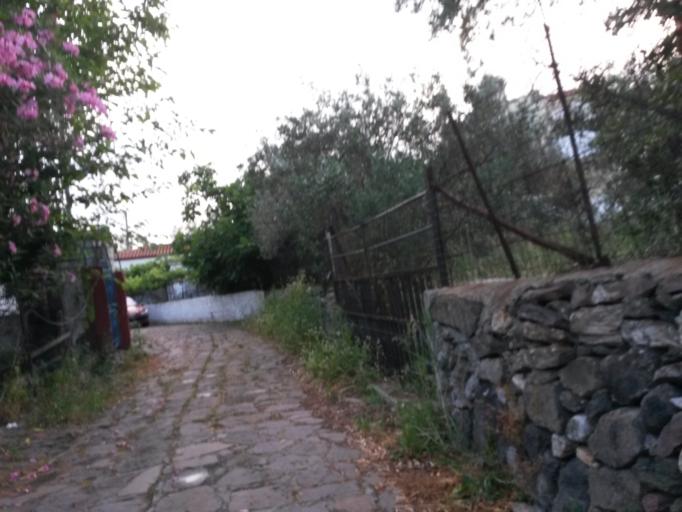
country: GR
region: North Aegean
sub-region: Nomos Lesvou
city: Pamfylla
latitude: 39.1758
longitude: 26.5027
